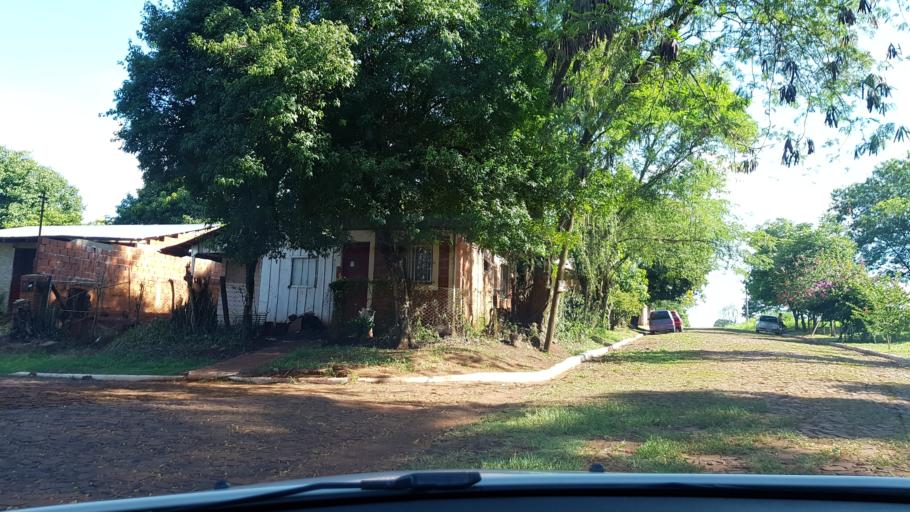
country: AR
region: Misiones
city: Puerto Libertad
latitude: -25.9216
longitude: -54.5897
